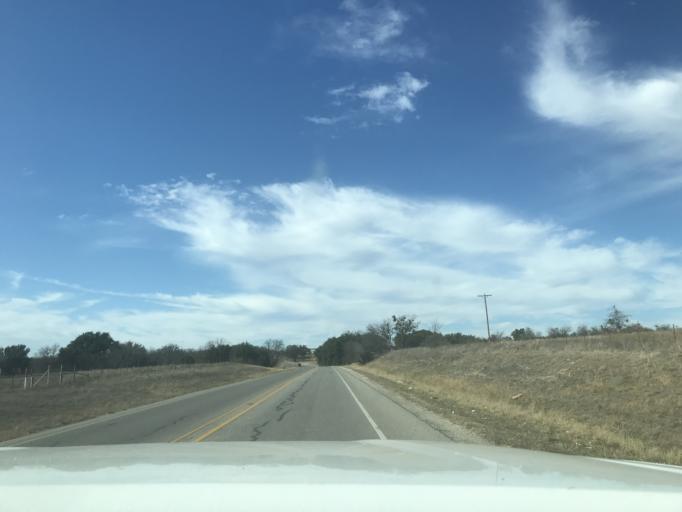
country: US
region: Texas
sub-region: Erath County
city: Stephenville
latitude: 32.2043
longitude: -98.1862
